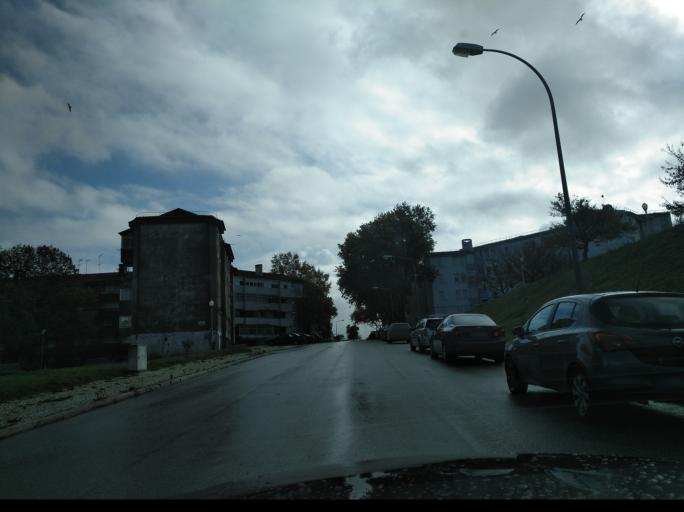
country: PT
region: Lisbon
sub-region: Loures
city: Moscavide
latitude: 38.7606
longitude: -9.1091
